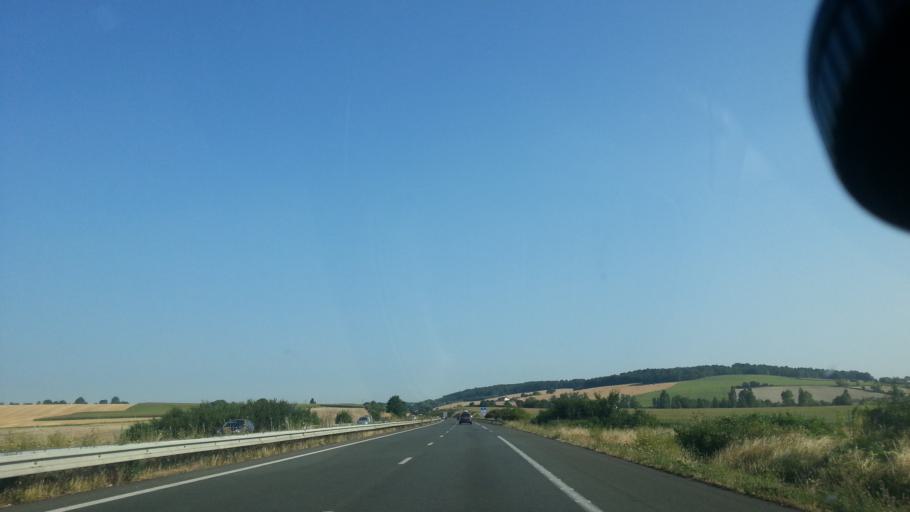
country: FR
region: Poitou-Charentes
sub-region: Departement de la Vienne
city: Antran
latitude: 46.8604
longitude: 0.5254
